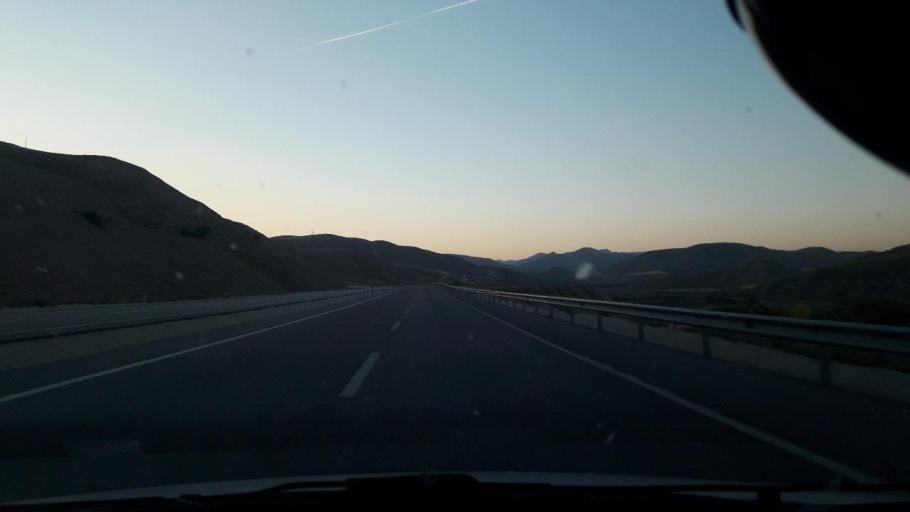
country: TR
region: Malatya
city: Yazihan
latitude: 38.6255
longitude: 38.1643
